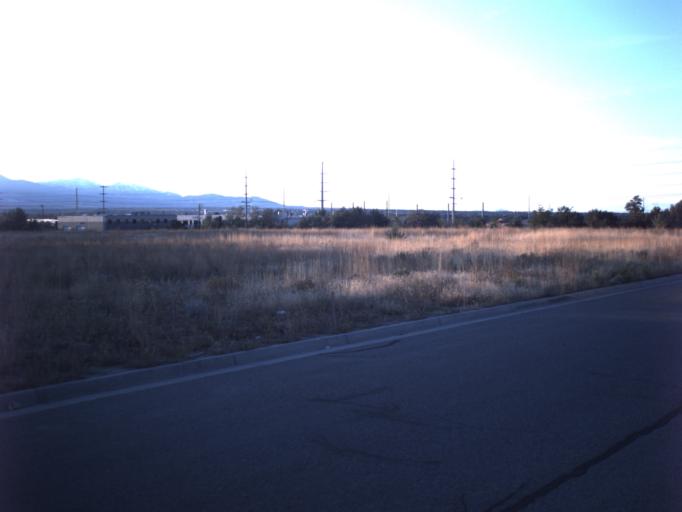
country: US
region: Utah
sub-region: Salt Lake County
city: Bluffdale
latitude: 40.4840
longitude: -111.9059
